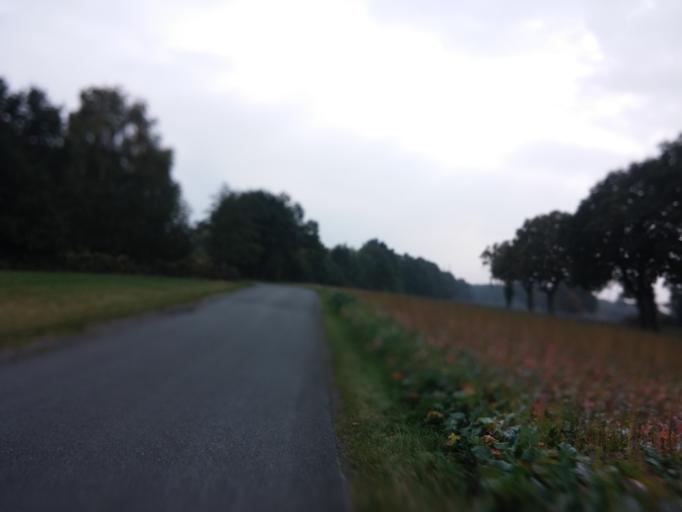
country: DE
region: North Rhine-Westphalia
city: Dorsten
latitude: 51.6430
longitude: 6.9691
